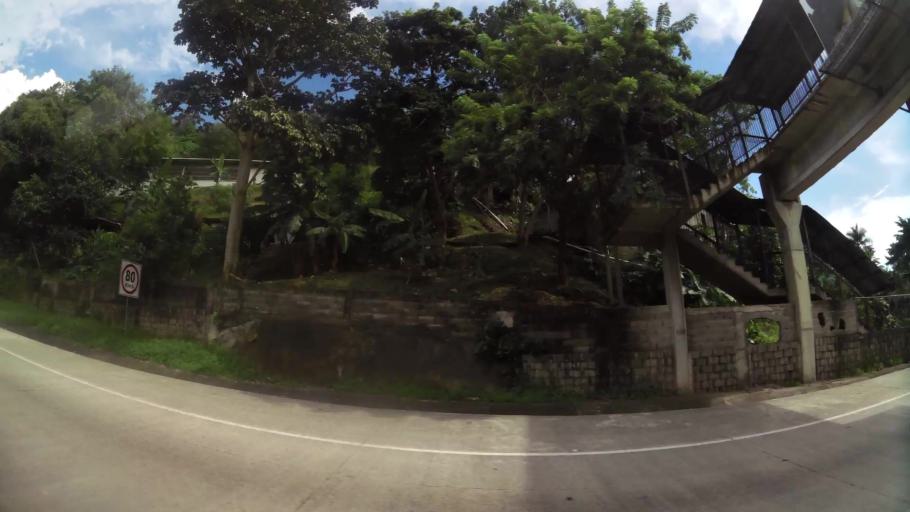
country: PA
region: Panama
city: San Miguelito
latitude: 9.0611
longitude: -79.5050
